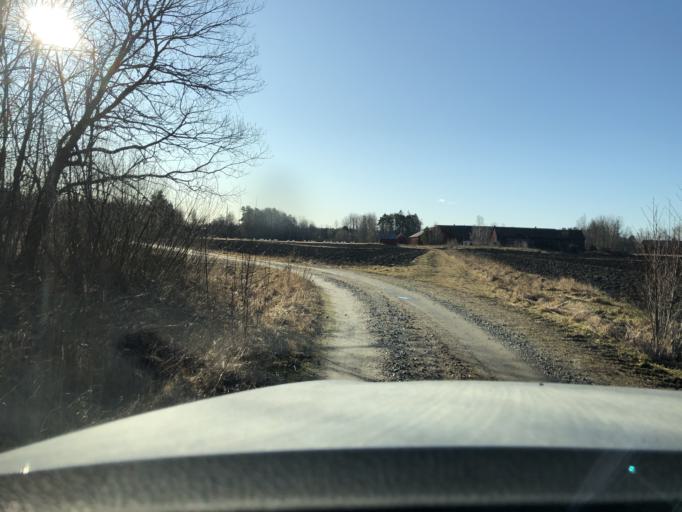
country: SE
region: Gaevleborg
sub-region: Gavle Kommun
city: Hedesunda
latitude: 60.2970
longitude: 16.8871
